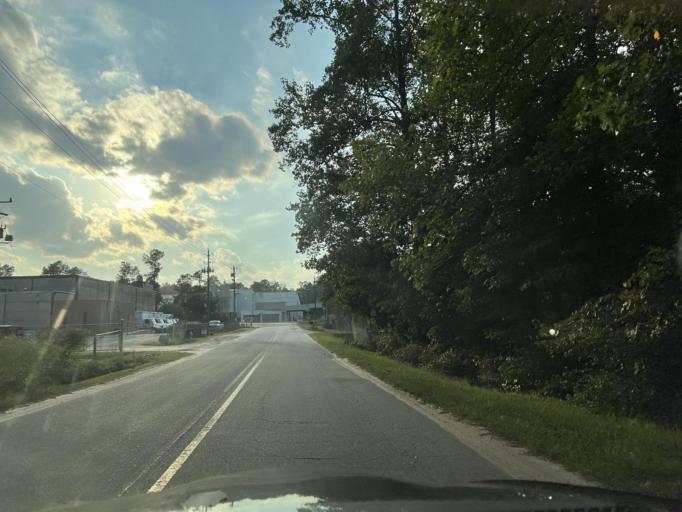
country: US
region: North Carolina
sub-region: Wake County
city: Raleigh
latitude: 35.7304
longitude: -78.6622
